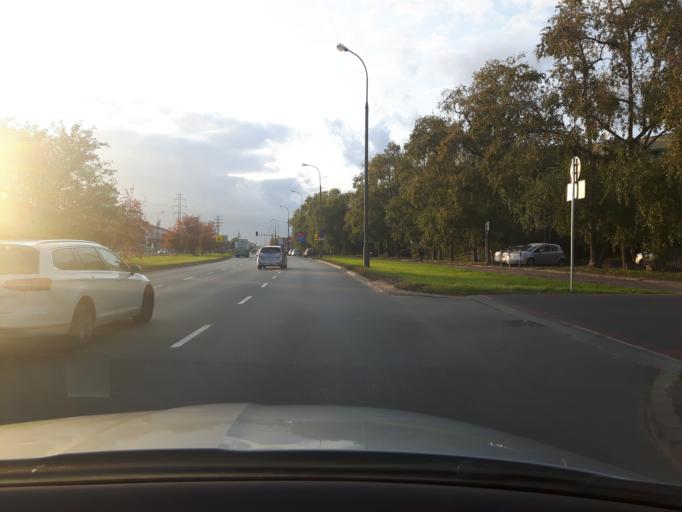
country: PL
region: Masovian Voivodeship
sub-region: Warszawa
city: Ursynow
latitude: 52.1507
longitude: 21.0298
